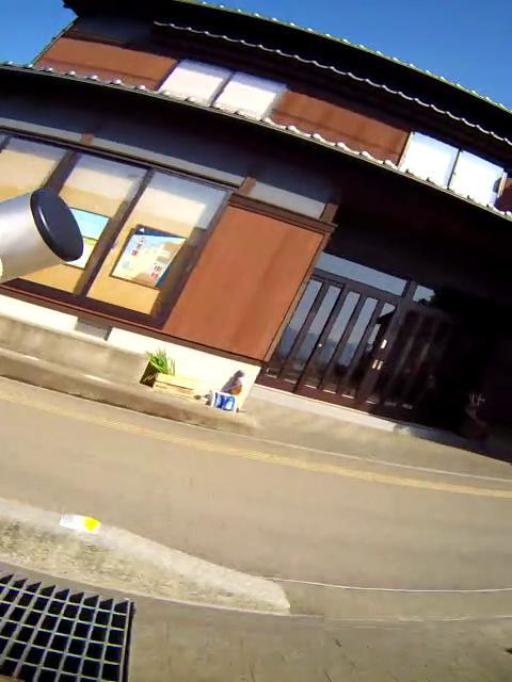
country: JP
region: Toyama
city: Nanto-shi
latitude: 36.5189
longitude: 136.9045
